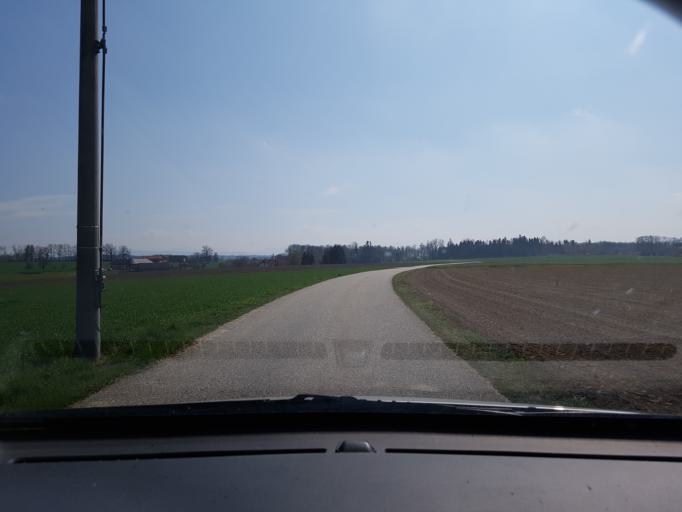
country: AT
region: Upper Austria
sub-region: Politischer Bezirk Linz-Land
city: Ansfelden
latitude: 48.1720
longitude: 14.3212
